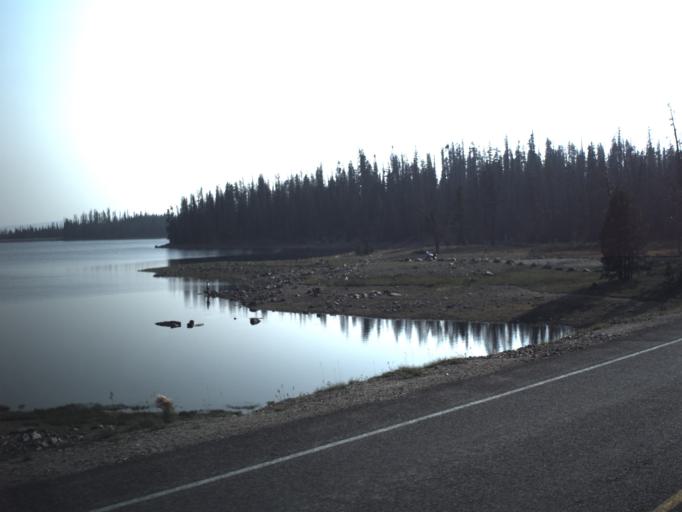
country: US
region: Utah
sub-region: Summit County
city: Kamas
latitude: 40.6810
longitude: -110.9365
